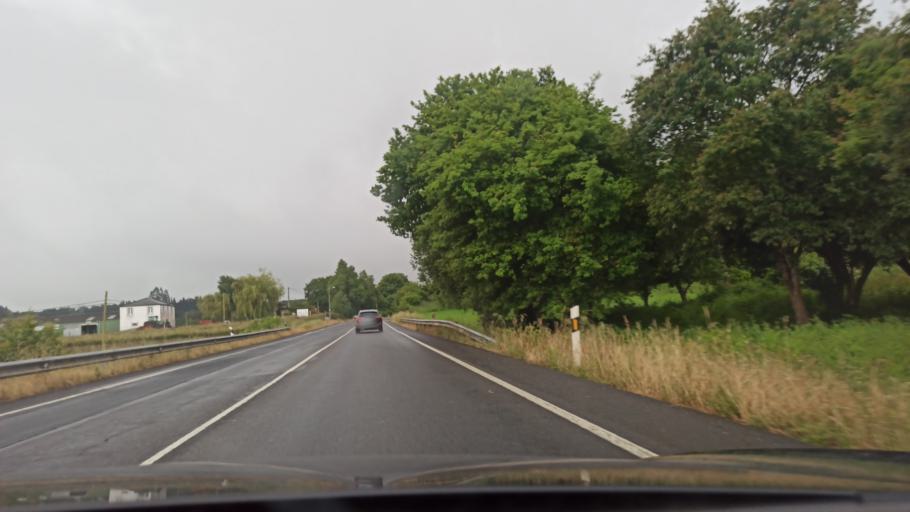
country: ES
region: Galicia
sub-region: Provincia de Lugo
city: Ourol
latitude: 42.9432
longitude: -7.6276
